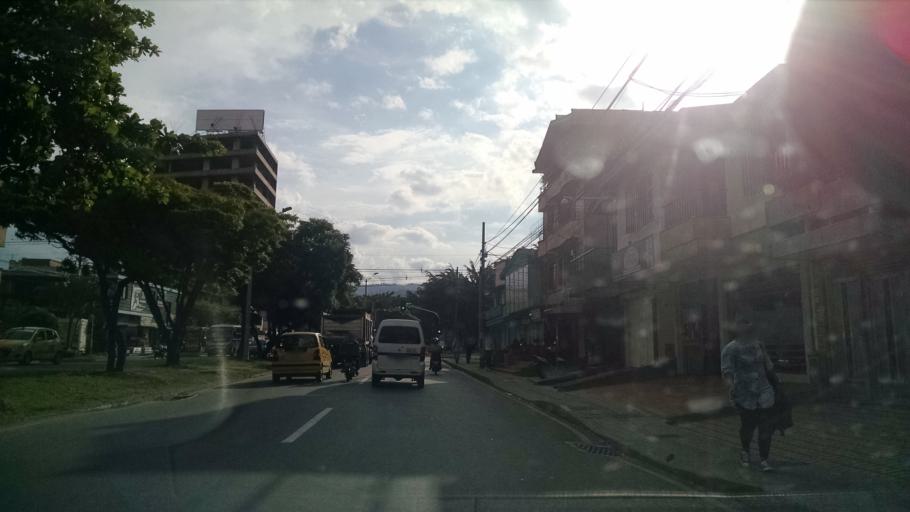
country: CO
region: Antioquia
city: Medellin
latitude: 6.2461
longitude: -75.5832
